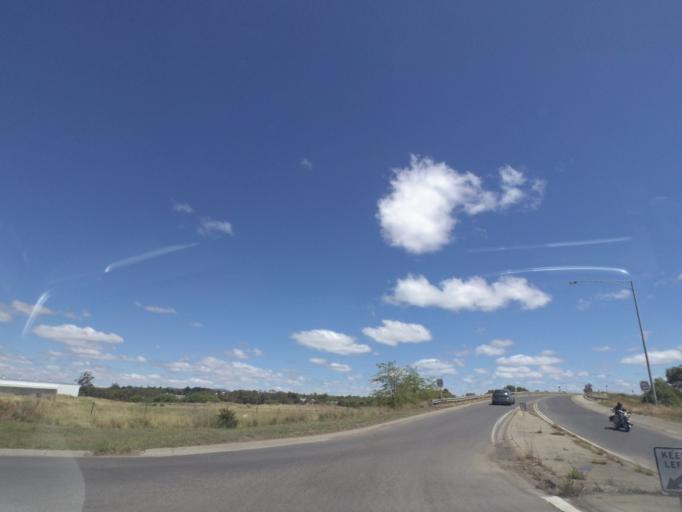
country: AU
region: Victoria
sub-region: Mount Alexander
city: Castlemaine
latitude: -37.2373
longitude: 144.4579
